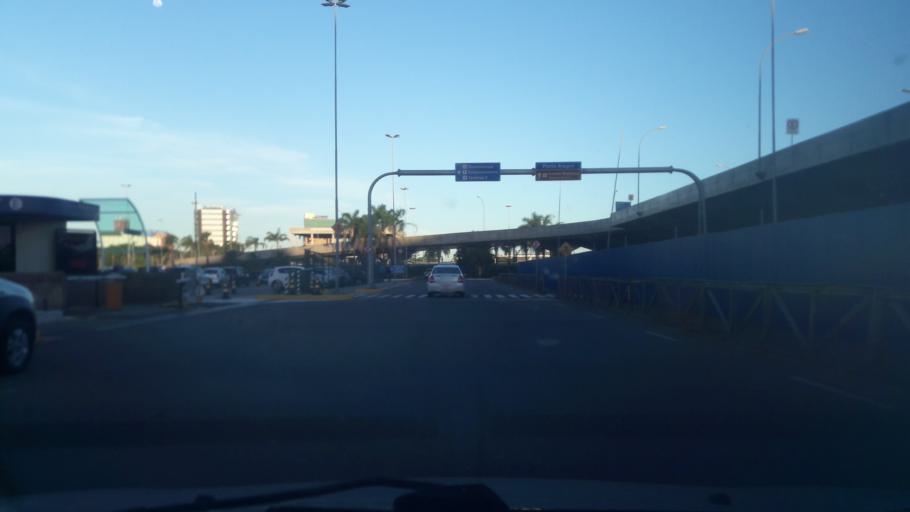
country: BR
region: Rio Grande do Sul
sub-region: Porto Alegre
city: Porto Alegre
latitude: -29.9897
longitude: -51.1753
